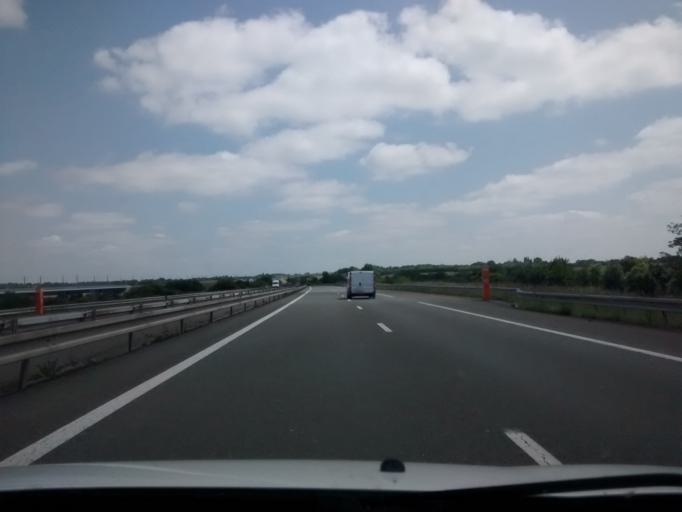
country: FR
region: Pays de la Loire
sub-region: Departement de la Mayenne
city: Louverne
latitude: 48.1014
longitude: -0.7260
